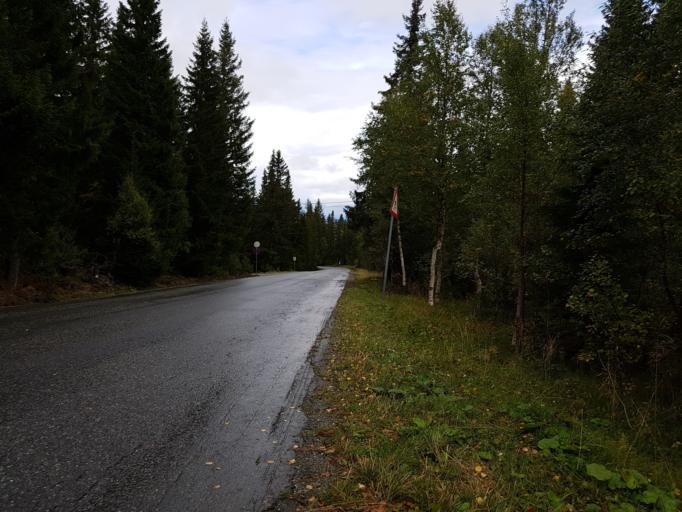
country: NO
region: Sor-Trondelag
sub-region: Trondheim
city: Trondheim
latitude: 63.4152
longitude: 10.2713
